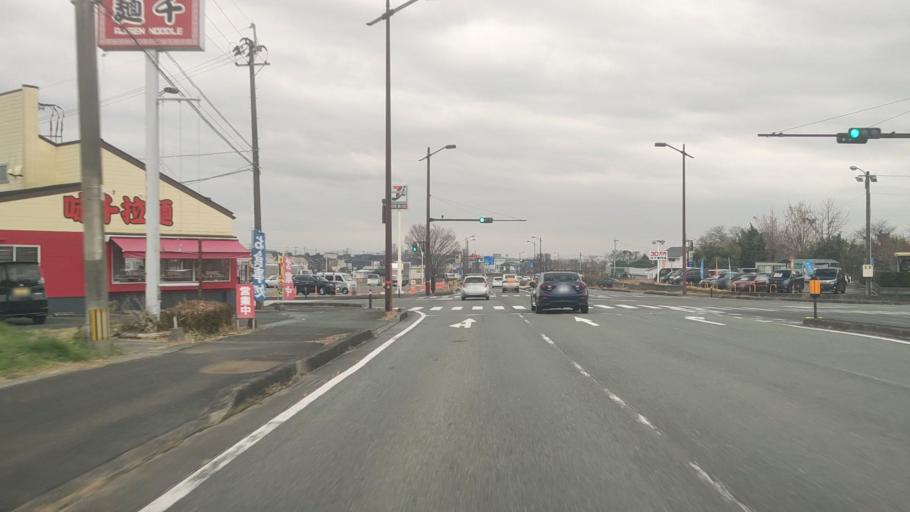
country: JP
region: Kumamoto
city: Ozu
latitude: 32.8310
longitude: 130.7983
